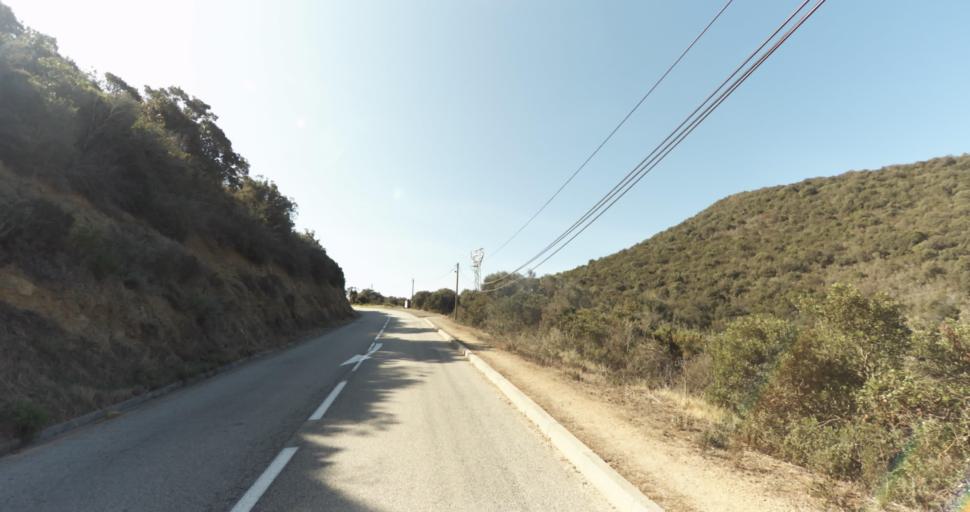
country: FR
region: Corsica
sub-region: Departement de la Corse-du-Sud
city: Ajaccio
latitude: 41.9236
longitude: 8.6425
